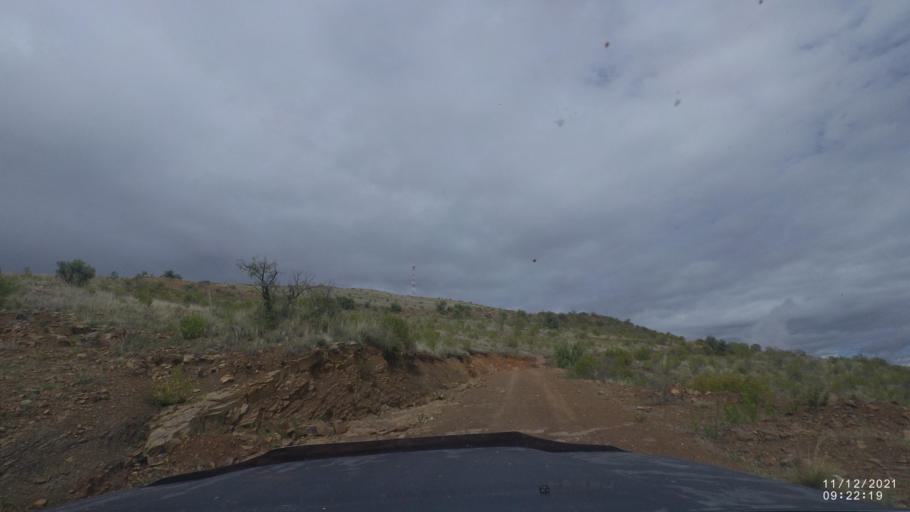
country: BO
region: Cochabamba
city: Tarata
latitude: -17.8785
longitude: -65.9756
